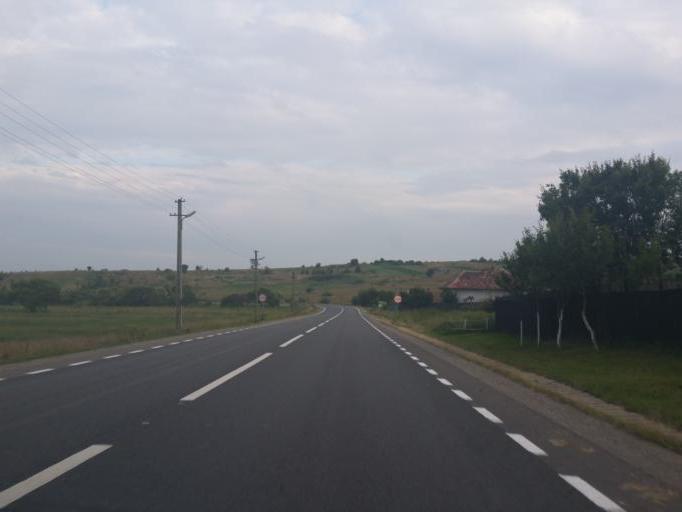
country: RO
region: Cluj
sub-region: Comuna Sanpaul
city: Sanpaul
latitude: 46.9293
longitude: 23.3973
